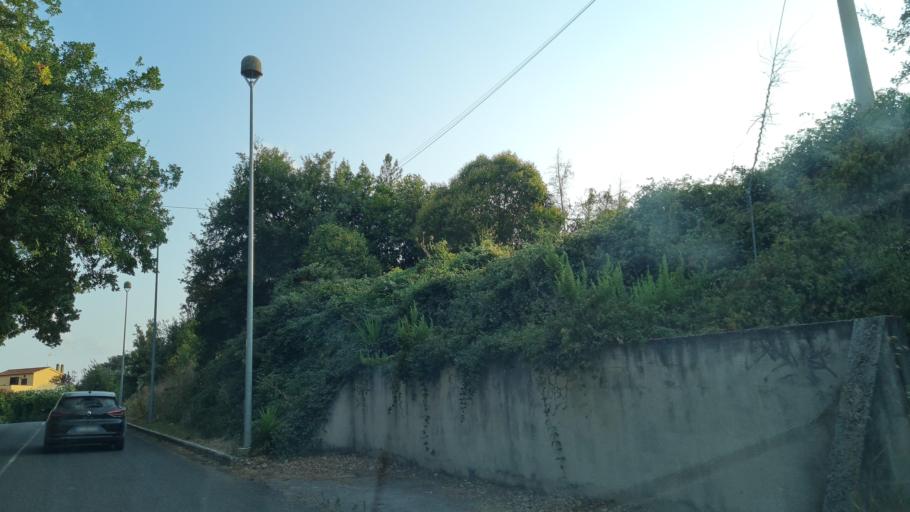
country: IT
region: Latium
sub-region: Provincia di Viterbo
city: Montalto di Castro
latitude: 42.3279
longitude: 11.6177
